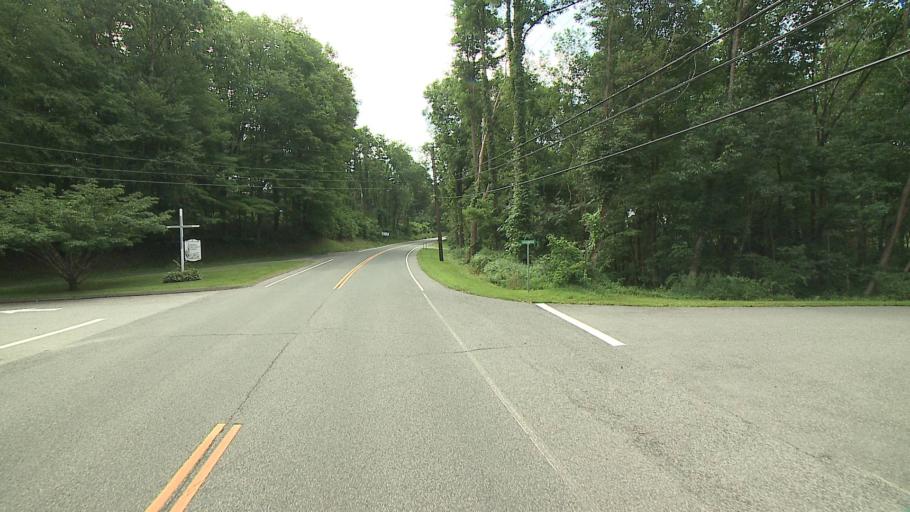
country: US
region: Connecticut
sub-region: Fairfield County
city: Sherman
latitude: 41.5951
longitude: -73.4976
